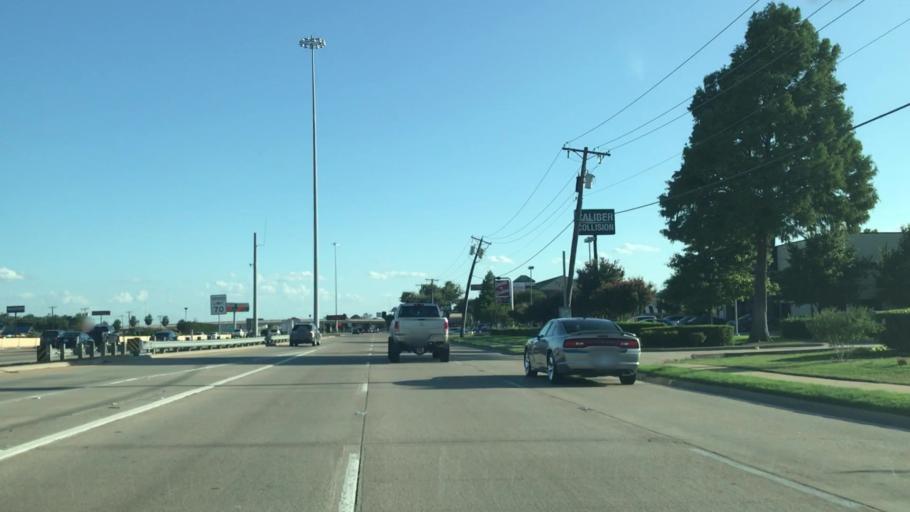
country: US
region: Texas
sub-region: Collin County
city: Plano
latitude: 33.0326
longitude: -96.7075
